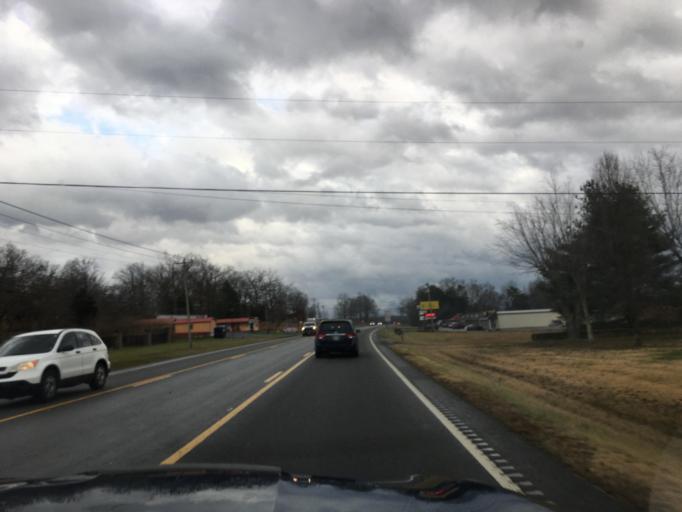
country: US
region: Tennessee
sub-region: Cumberland County
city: Crossville
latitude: 35.9239
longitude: -85.0025
